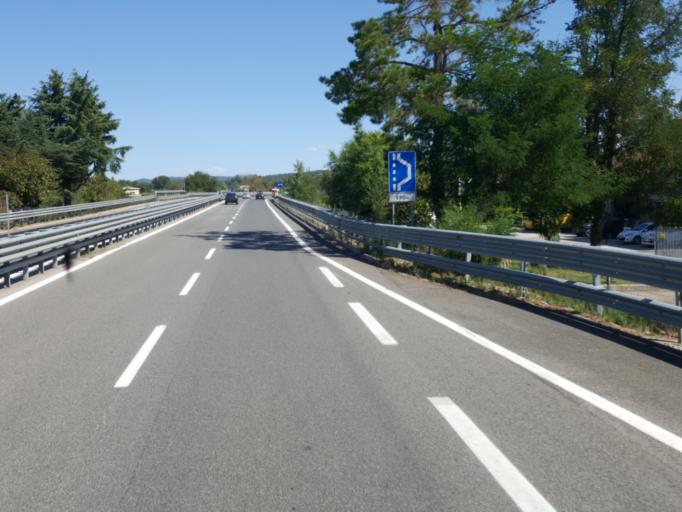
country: IT
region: Tuscany
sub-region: Provincia di Grosseto
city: Campagnatico
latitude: 42.9298
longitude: 11.2659
